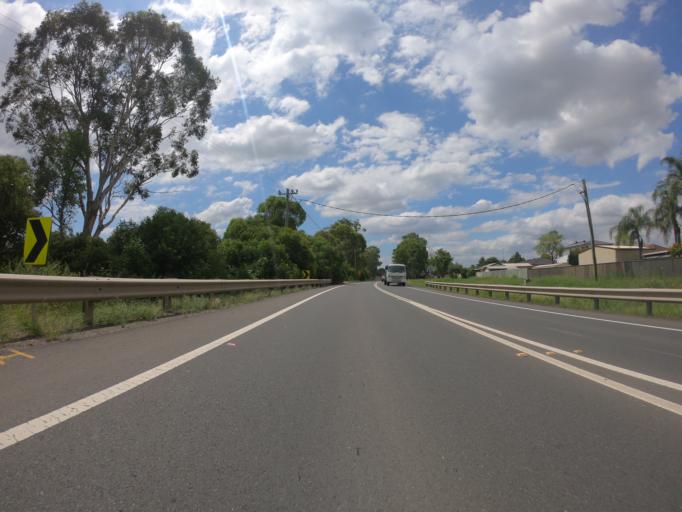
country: AU
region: New South Wales
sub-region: Blacktown
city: Mount Druitt
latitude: -33.8007
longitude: 150.7683
